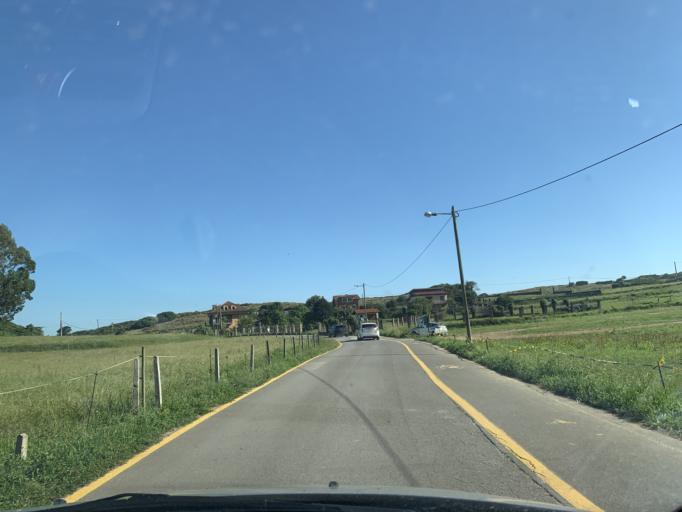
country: ES
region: Asturias
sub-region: Province of Asturias
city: Llanes
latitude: 43.4270
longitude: -4.7825
